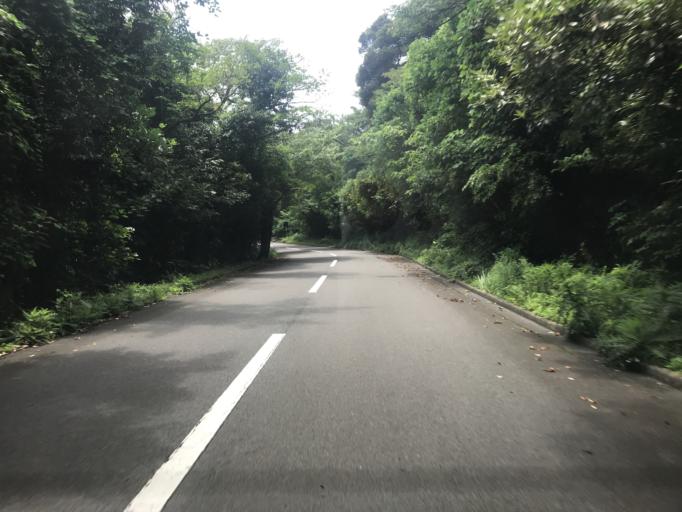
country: JP
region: Shizuoka
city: Ito
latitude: 34.7638
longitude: 139.4285
